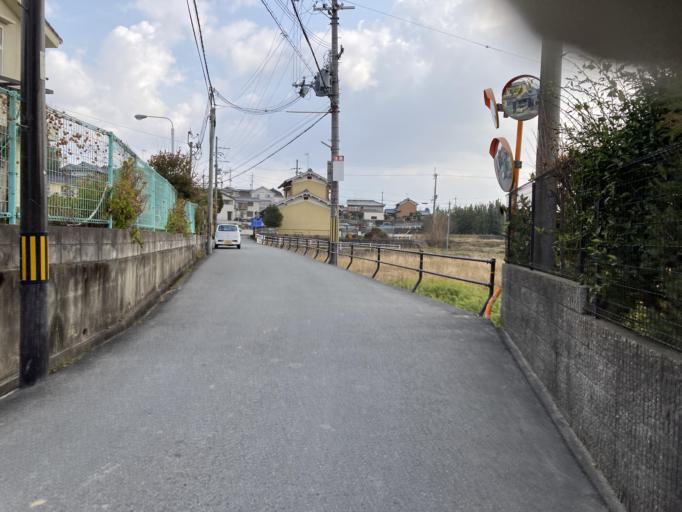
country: JP
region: Nara
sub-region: Ikoma-shi
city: Ikoma
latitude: 34.6095
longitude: 135.7170
